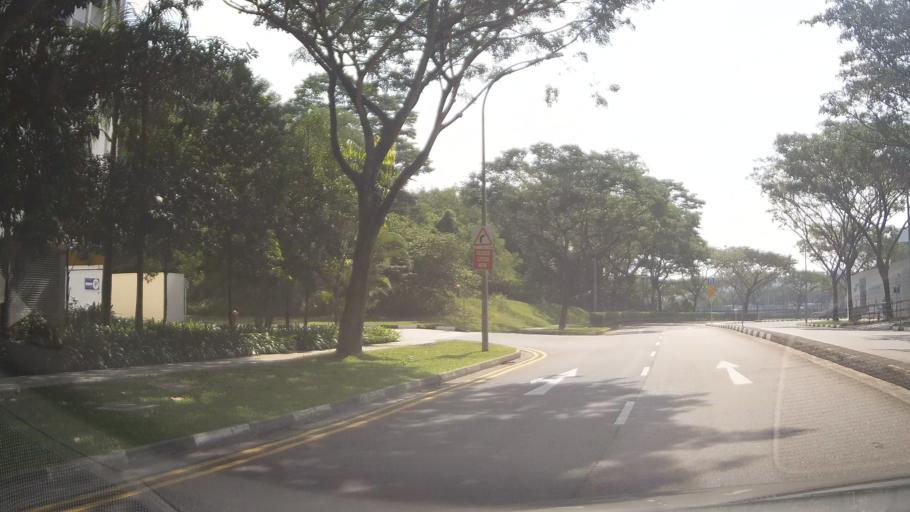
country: MY
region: Johor
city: Johor Bahru
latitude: 1.3545
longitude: 103.6931
